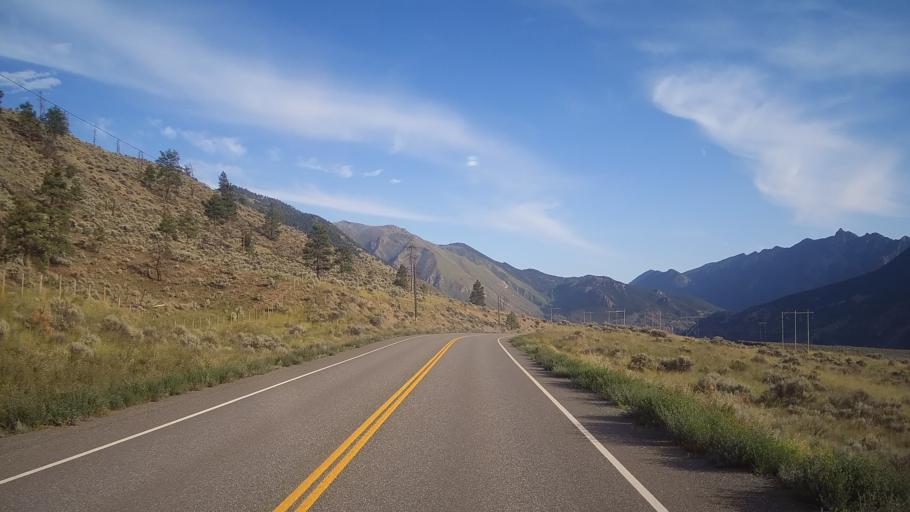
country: CA
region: British Columbia
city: Lillooet
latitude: 50.8115
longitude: -121.8497
